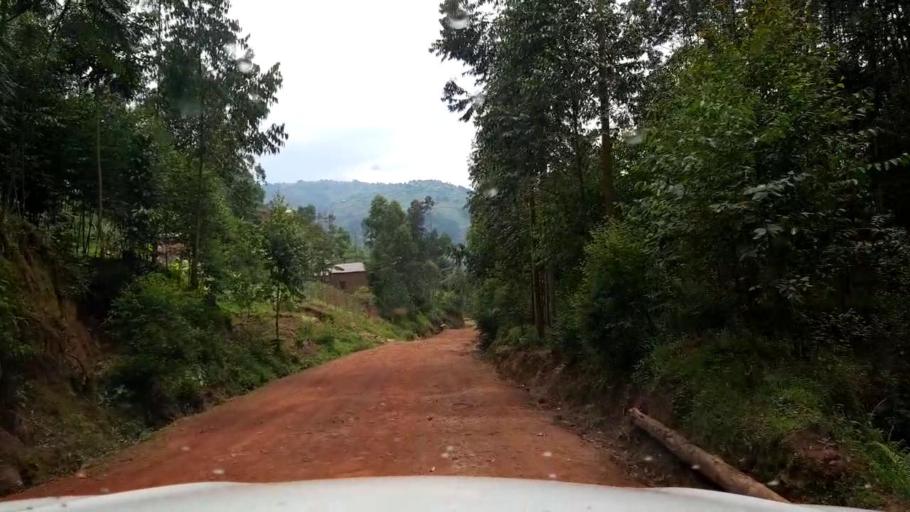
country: RW
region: Northern Province
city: Byumba
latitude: -1.5328
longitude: 30.0115
